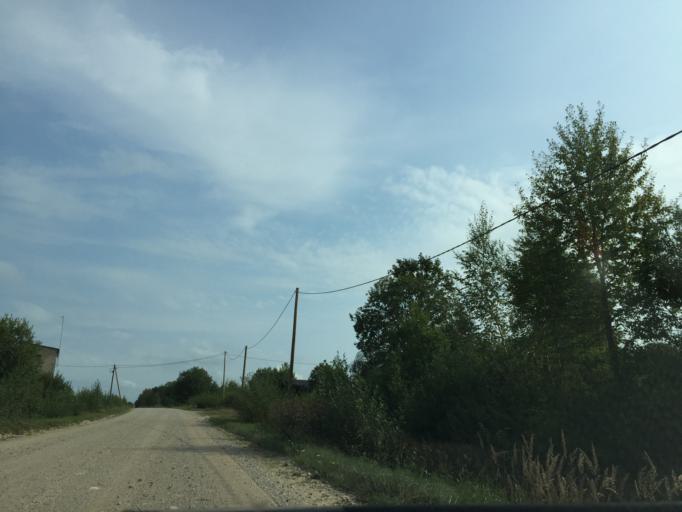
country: LV
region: Cibla
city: Cibla
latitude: 56.2743
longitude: 27.8033
